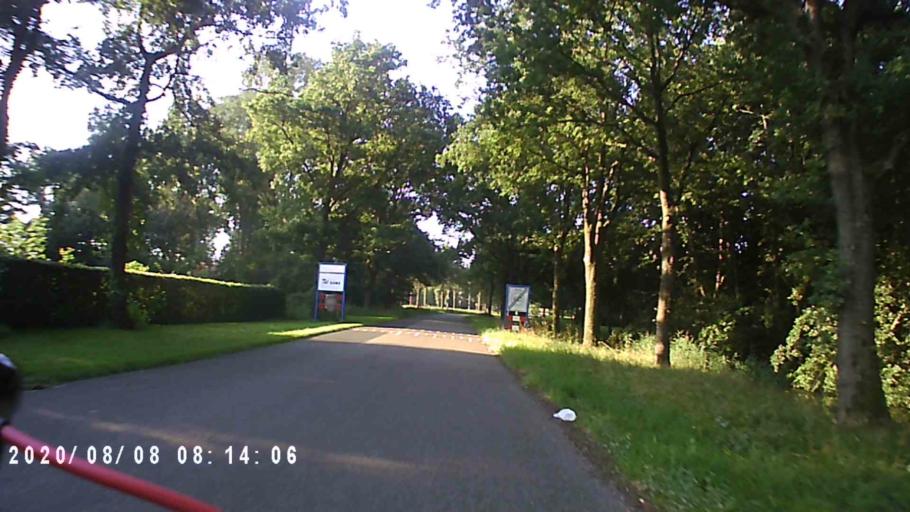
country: NL
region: Groningen
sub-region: Gemeente Leek
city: Leek
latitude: 53.0975
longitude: 6.3410
